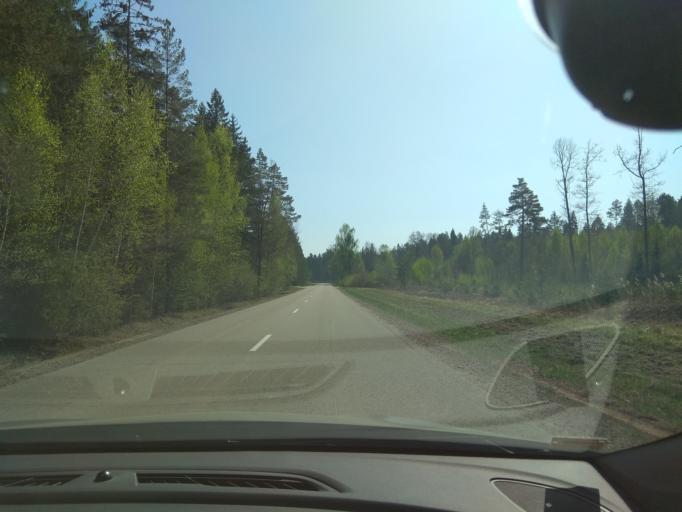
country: LT
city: Linkuva
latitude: 55.9866
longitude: 24.1771
